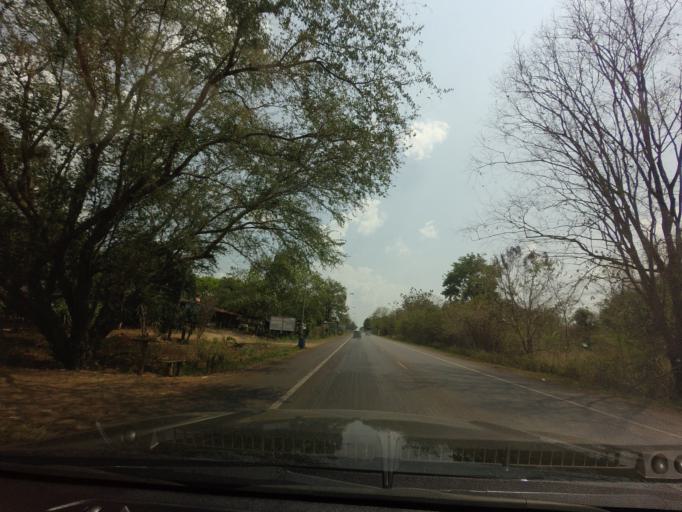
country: TH
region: Kanchanaburi
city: Sai Yok
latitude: 14.1330
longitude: 99.1581
